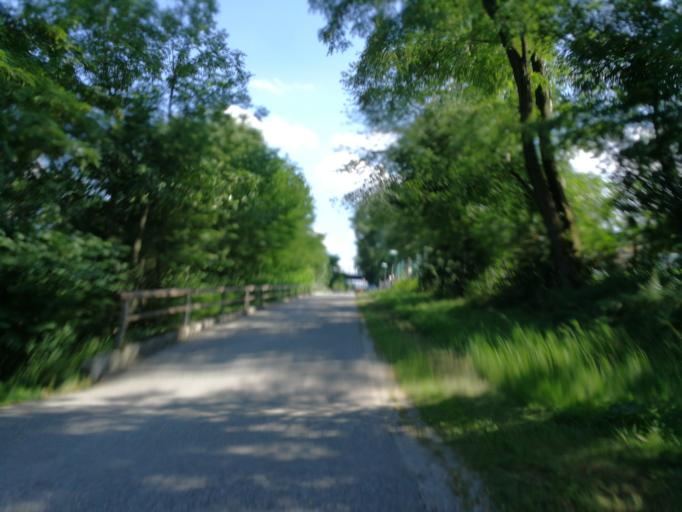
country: AT
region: Salzburg
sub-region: Politischer Bezirk Salzburg-Umgebung
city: Bergheim
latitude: 47.8296
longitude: 13.0285
